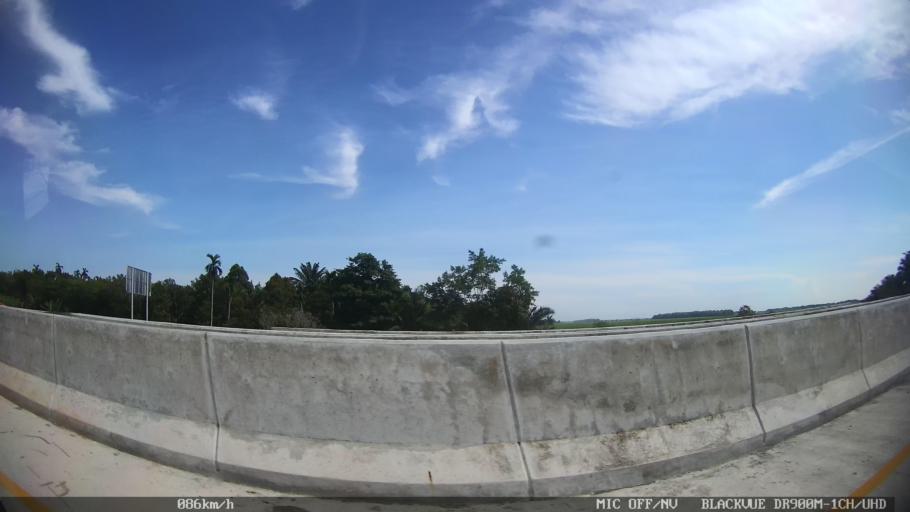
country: ID
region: North Sumatra
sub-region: Kabupaten Langkat
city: Stabat
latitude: 3.7132
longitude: 98.5101
